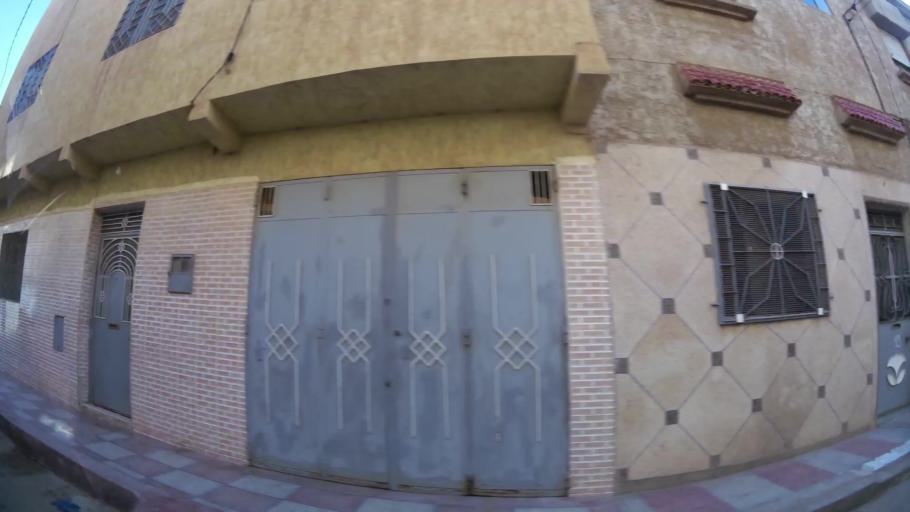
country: MA
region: Oriental
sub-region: Oujda-Angad
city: Oujda
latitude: 34.7103
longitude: -1.8906
